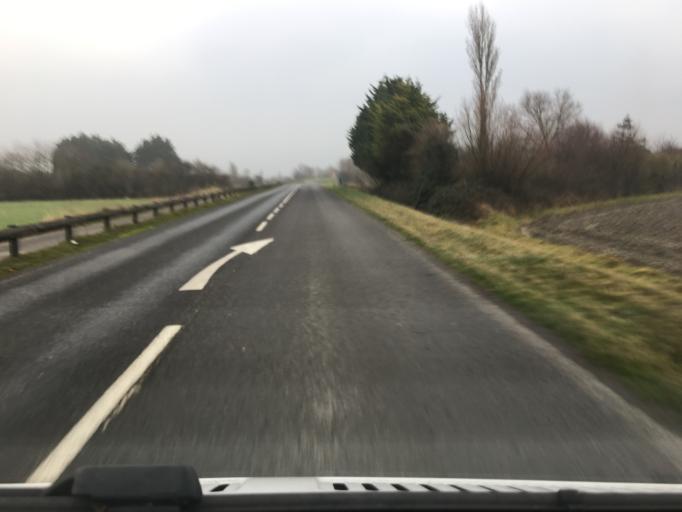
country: FR
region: Picardie
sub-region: Departement de la Somme
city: Le Crotoy
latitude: 50.2248
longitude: 1.6311
